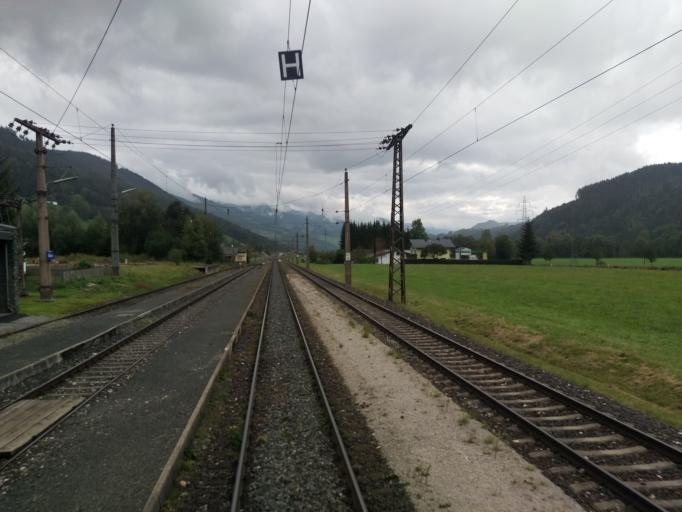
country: AT
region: Styria
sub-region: Politischer Bezirk Liezen
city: Oblarn
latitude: 47.4609
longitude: 13.9879
